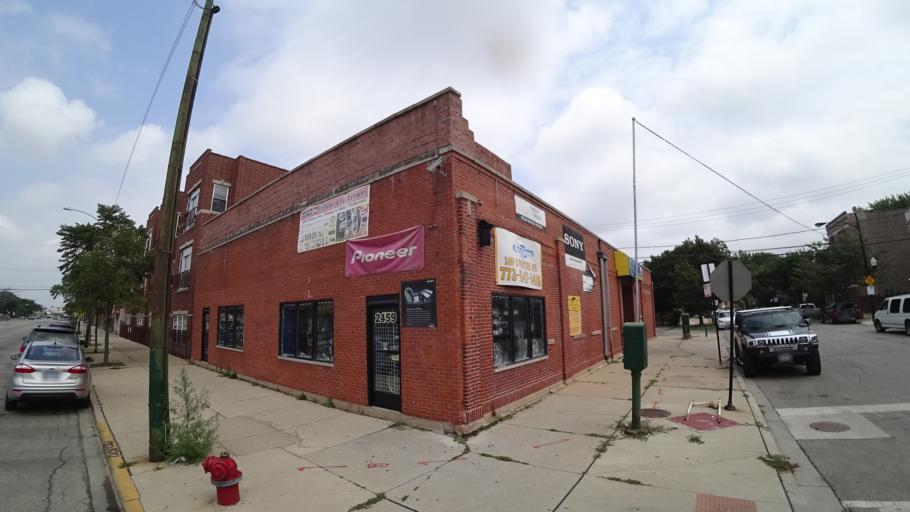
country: US
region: Illinois
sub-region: Cook County
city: Chicago
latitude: 41.8466
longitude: -87.6854
